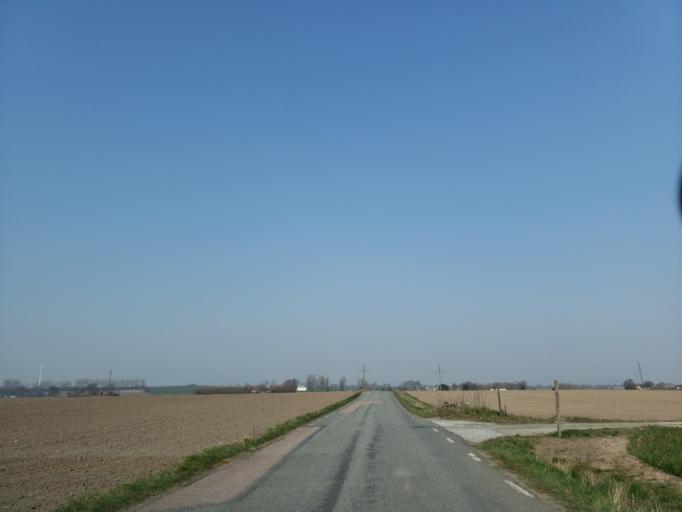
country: SE
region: Skane
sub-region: Simrishamns Kommun
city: Simrishamn
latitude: 55.4597
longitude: 14.2120
